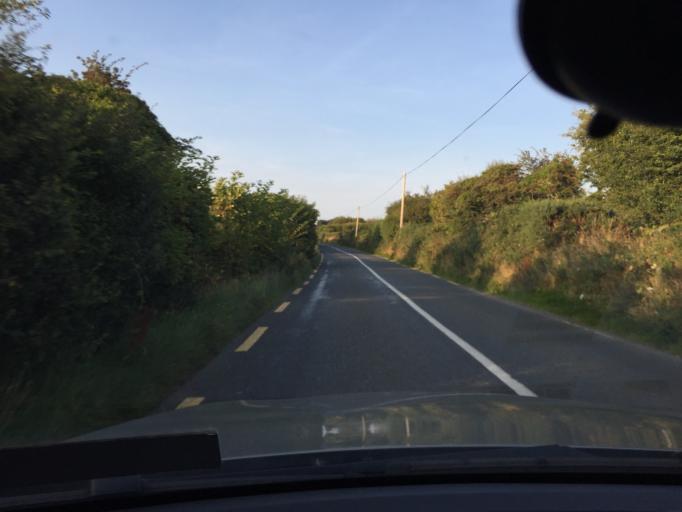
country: IE
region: Leinster
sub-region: Wicklow
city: Rathdrum
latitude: 53.0501
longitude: -6.2392
